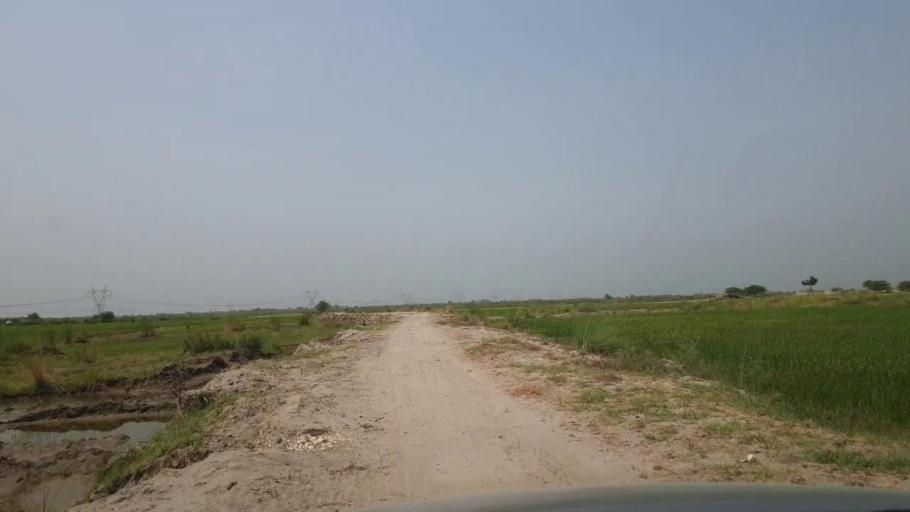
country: PK
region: Sindh
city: Madeji
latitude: 27.8145
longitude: 68.5131
